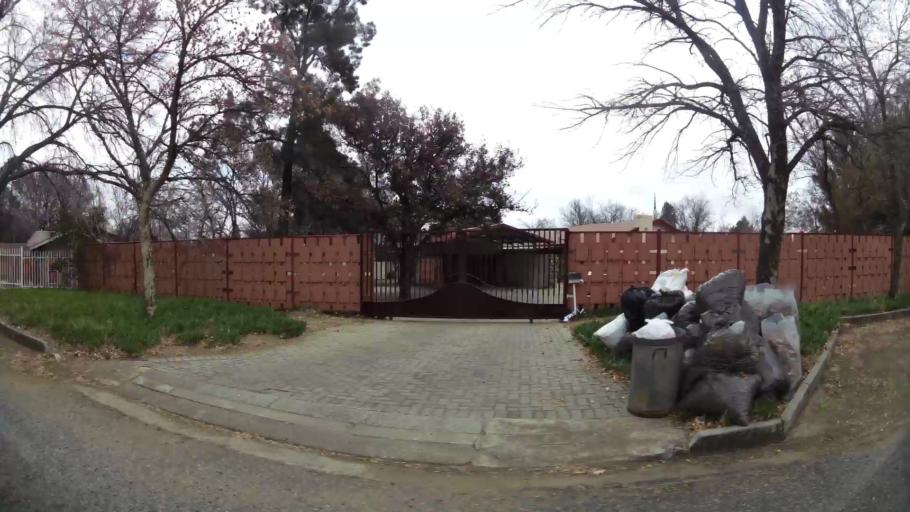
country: ZA
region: Orange Free State
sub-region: Fezile Dabi District Municipality
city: Kroonstad
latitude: -27.6722
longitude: 27.2493
